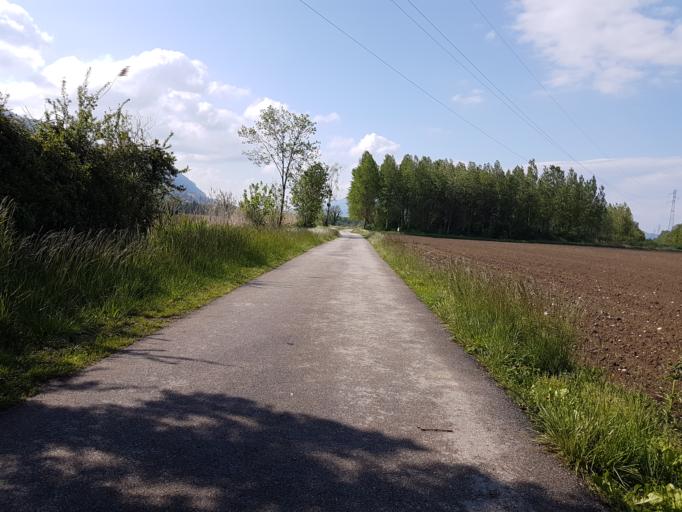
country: FR
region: Rhone-Alpes
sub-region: Departement de l'Ain
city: Culoz
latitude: 45.8801
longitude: 5.8337
